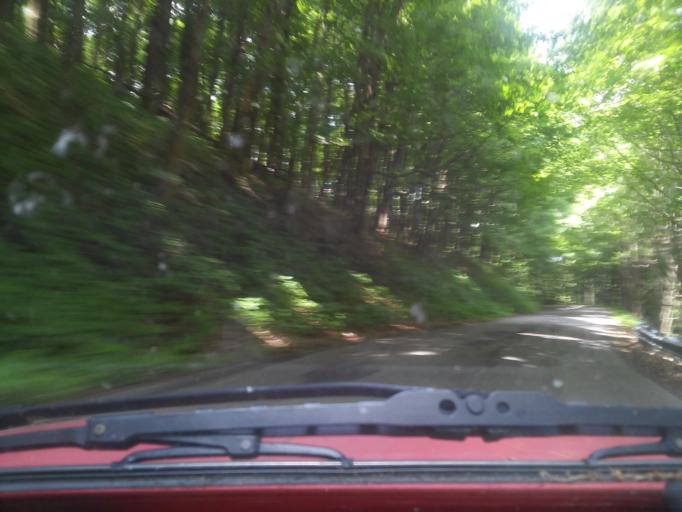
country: US
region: Virginia
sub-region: Giles County
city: Pembroke
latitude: 37.3384
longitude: -80.5550
